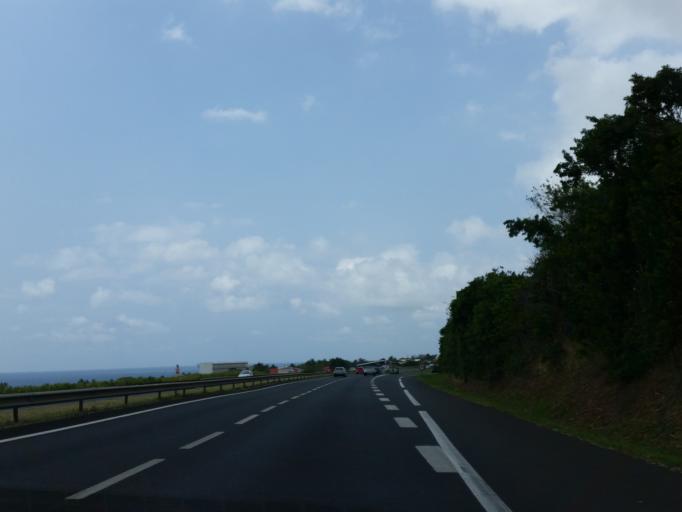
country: RE
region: Reunion
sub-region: Reunion
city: Sainte-Suzanne
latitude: -20.9016
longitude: 55.5926
